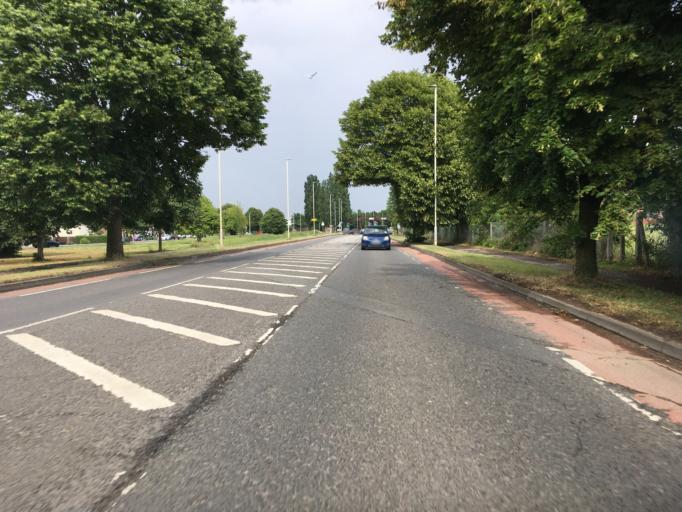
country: GB
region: England
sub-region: Gloucestershire
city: Gloucester
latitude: 51.8373
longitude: -2.2597
